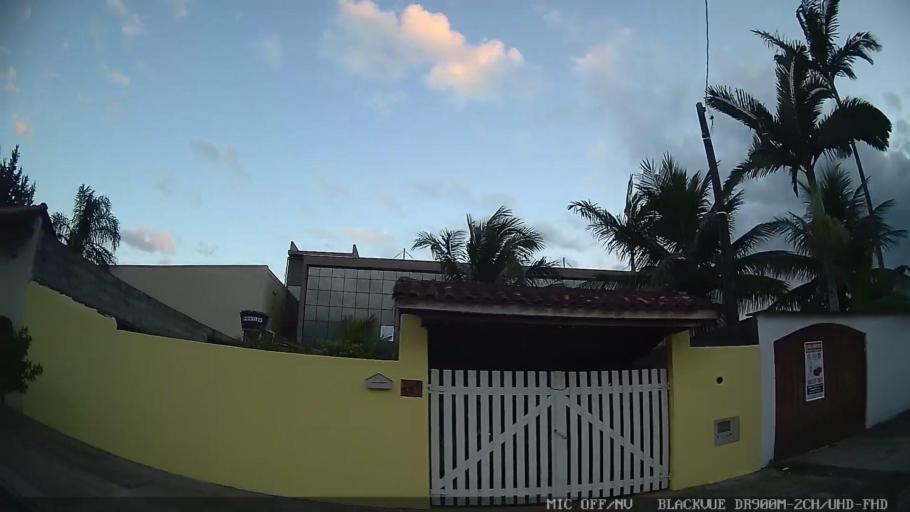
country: BR
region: Sao Paulo
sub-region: Caraguatatuba
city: Caraguatatuba
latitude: -23.6653
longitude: -45.4441
